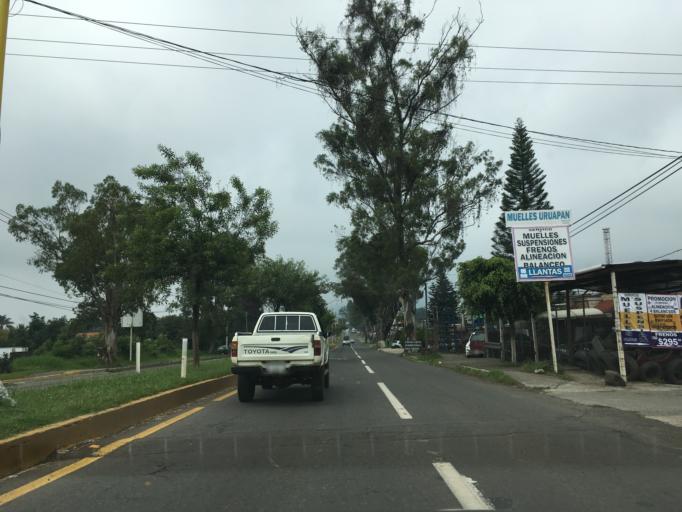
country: MX
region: Michoacan
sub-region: Uruapan
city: Toreo Bajo (El Toreo Bajo)
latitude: 19.4213
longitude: -102.0041
